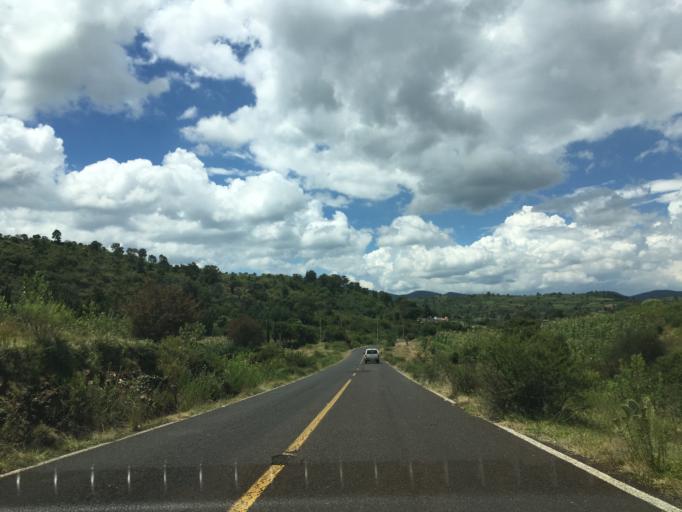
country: MX
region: Michoacan
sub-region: Morelia
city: Cuto de la Esperanza
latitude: 19.7780
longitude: -101.4265
